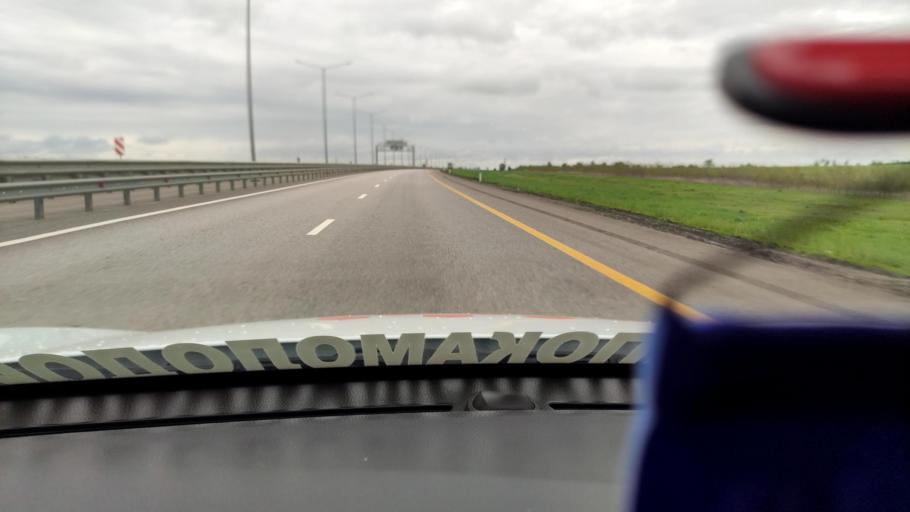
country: RU
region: Voronezj
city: Novaya Usman'
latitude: 51.6015
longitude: 39.3430
